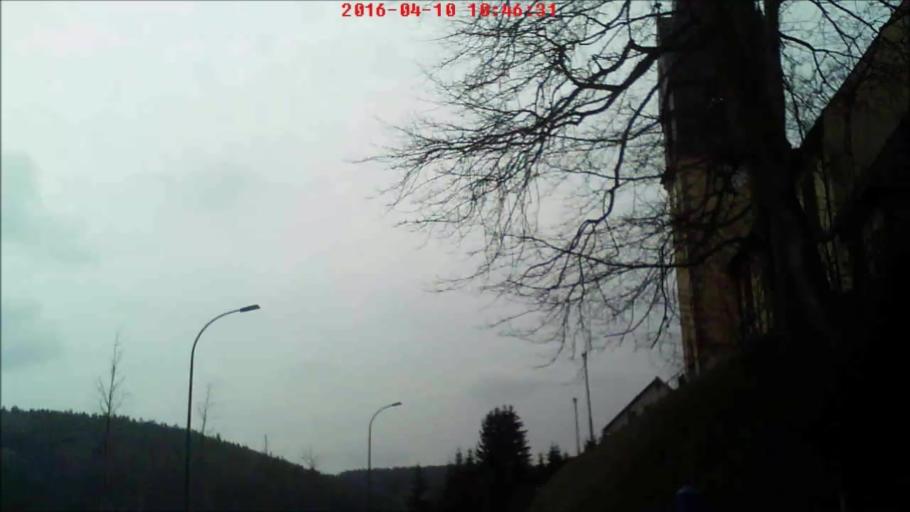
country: DE
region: Thuringia
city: Stutzerbach
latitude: 50.6347
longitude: 10.8609
